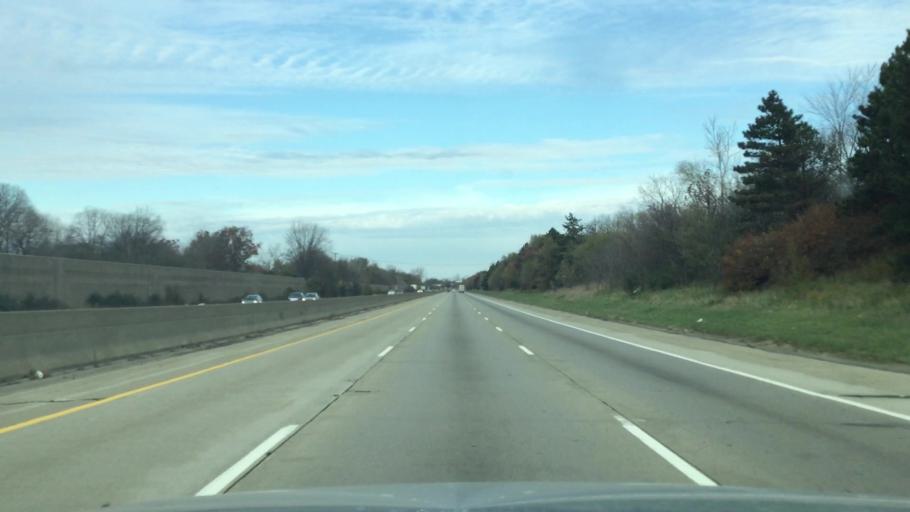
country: US
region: Michigan
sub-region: Washtenaw County
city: Ypsilanti
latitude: 42.2227
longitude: -83.5657
